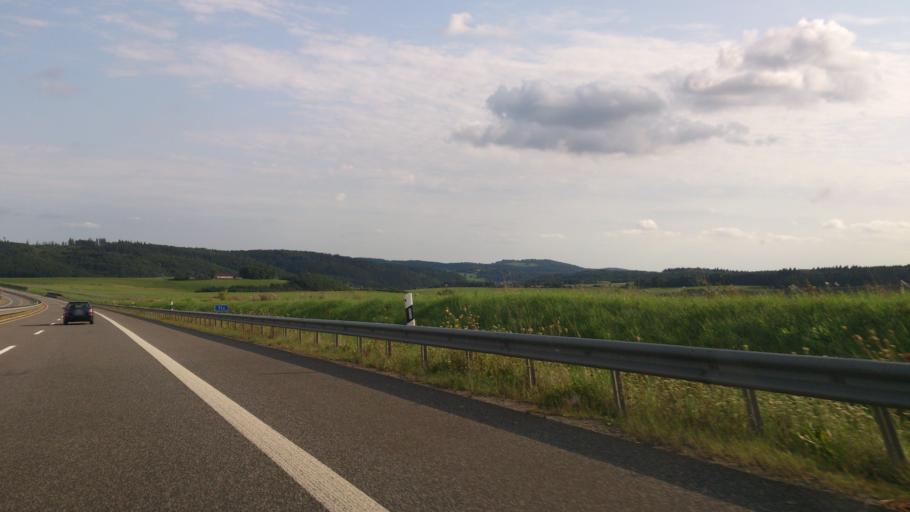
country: DE
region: Rheinland-Pfalz
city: Kradenbach
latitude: 50.2411
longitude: 6.8345
